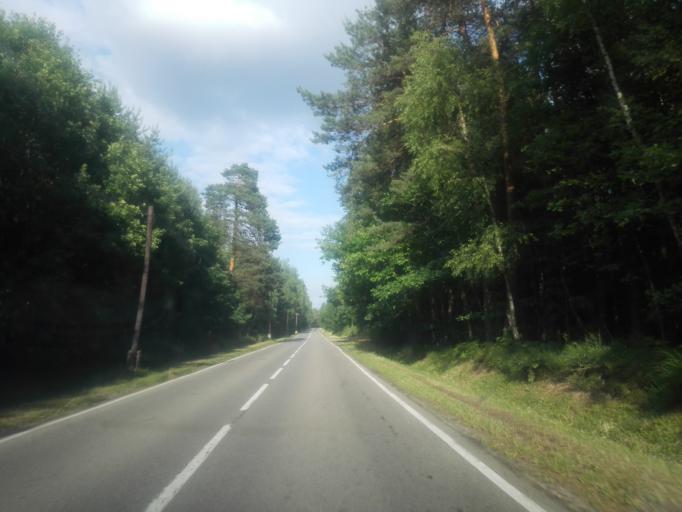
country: PL
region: Silesian Voivodeship
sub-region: Powiat czestochowski
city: Potok Zloty
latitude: 50.7069
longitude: 19.5164
